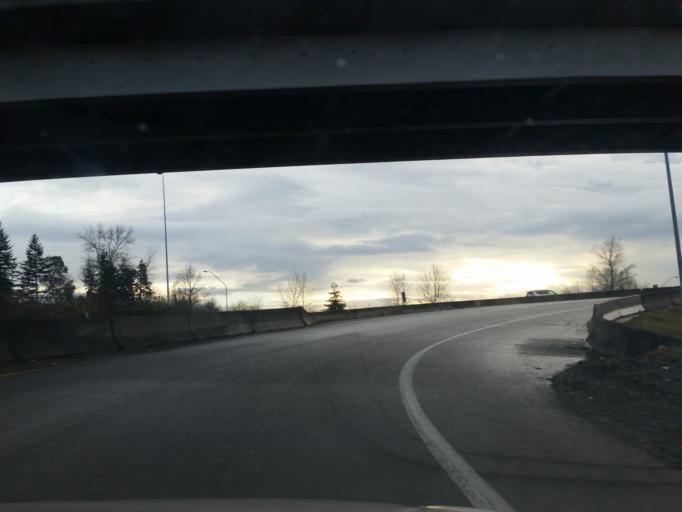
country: US
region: Washington
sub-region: King County
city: Renton
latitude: 47.4686
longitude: -122.2164
